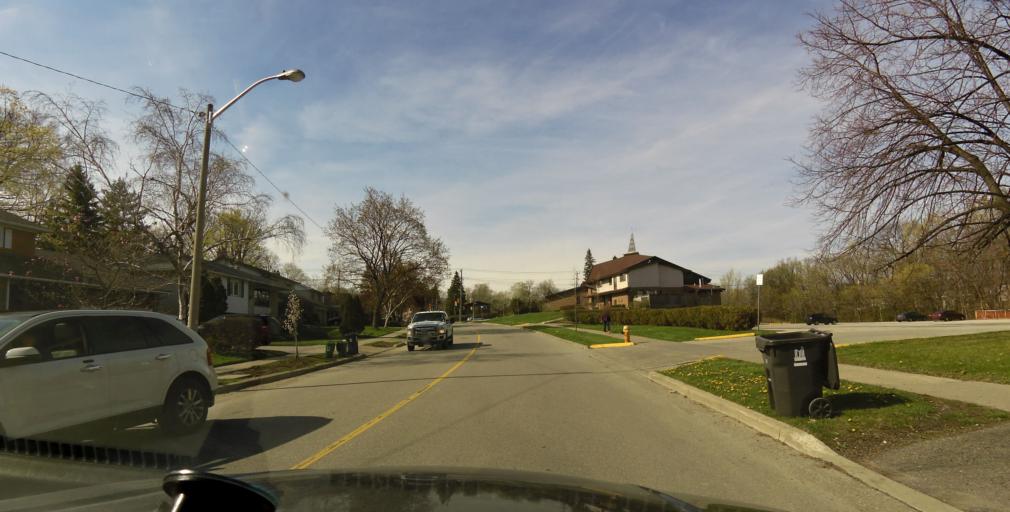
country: CA
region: Ontario
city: Etobicoke
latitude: 43.6323
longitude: -79.5704
